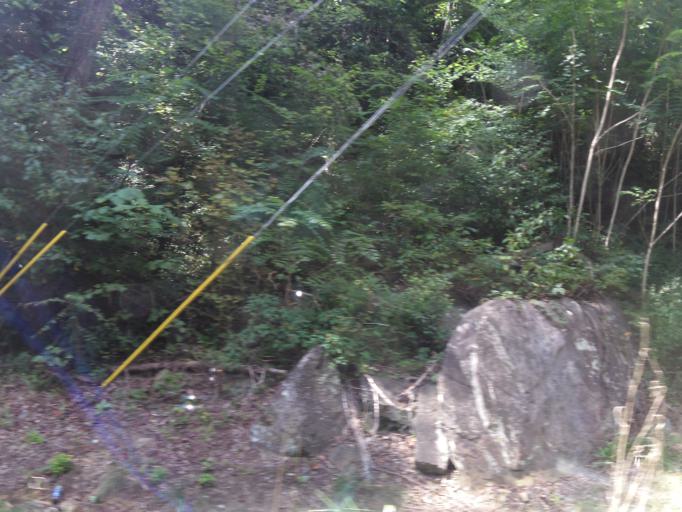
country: US
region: Kentucky
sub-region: Harlan County
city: Harlan
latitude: 36.8761
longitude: -83.3209
